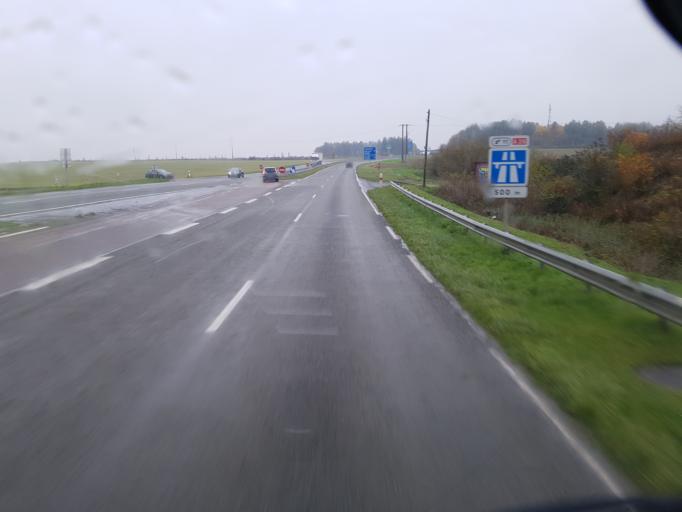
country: FR
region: Picardie
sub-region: Departement de l'Aisne
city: Gauchy
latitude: 49.8092
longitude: 3.2868
